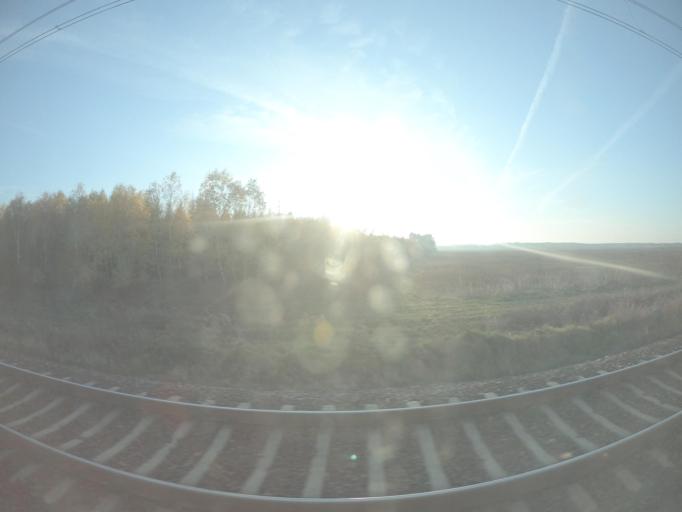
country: PL
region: Lubusz
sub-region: Powiat slubicki
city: Rzepin
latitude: 52.2896
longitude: 14.8902
